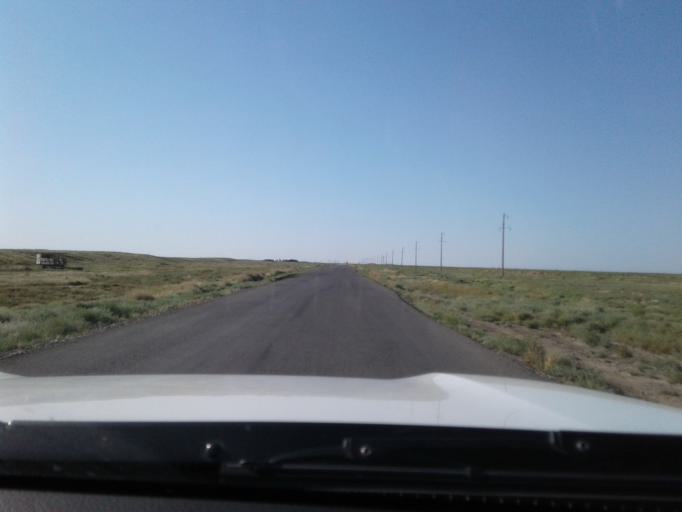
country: IR
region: Razavi Khorasan
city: Kalat-e Naderi
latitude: 37.1611
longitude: 60.0502
